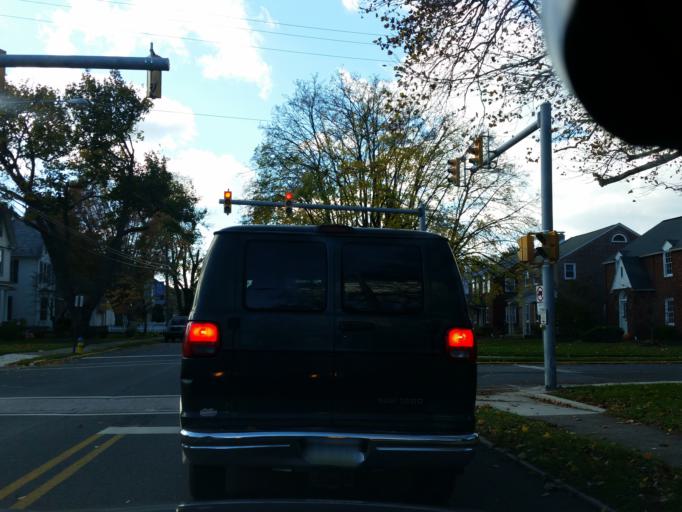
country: US
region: Pennsylvania
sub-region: Cumberland County
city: Camp Hill
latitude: 40.2404
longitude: -76.9297
